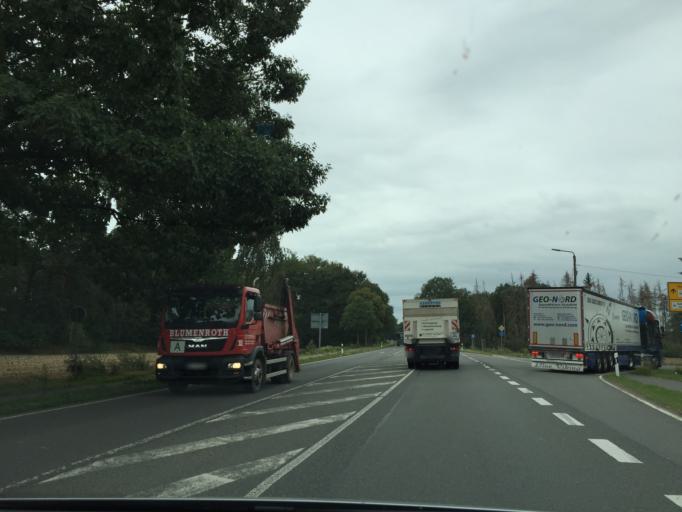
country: DE
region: North Rhine-Westphalia
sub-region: Regierungsbezirk Dusseldorf
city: Voerde
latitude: 51.6375
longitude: 6.7184
